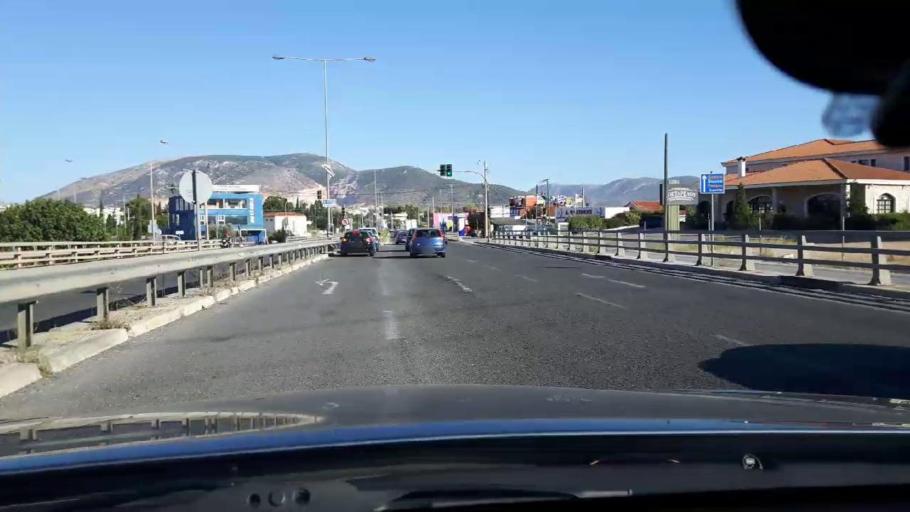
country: GR
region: Attica
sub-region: Nomarchia Anatolikis Attikis
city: Markopoulo
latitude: 37.8885
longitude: 23.9236
